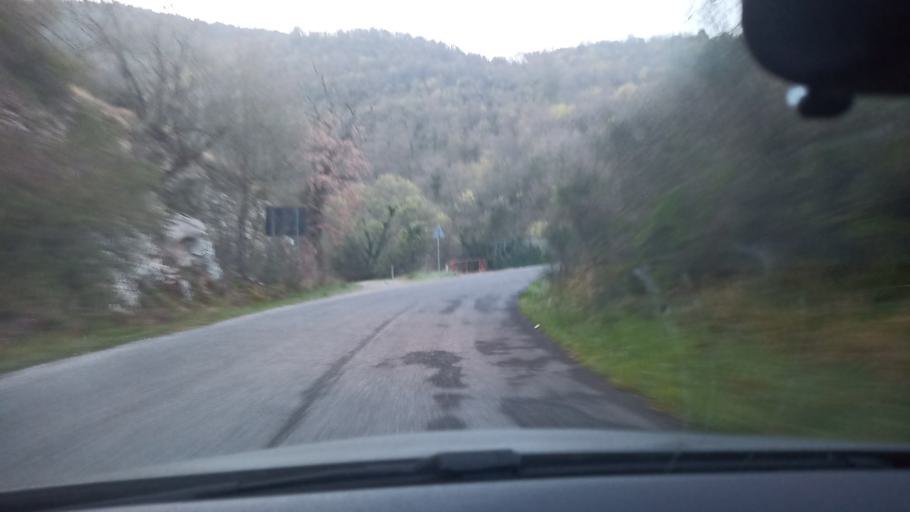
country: IT
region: Latium
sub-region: Provincia di Rieti
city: Cottanello
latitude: 42.4030
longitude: 12.6817
